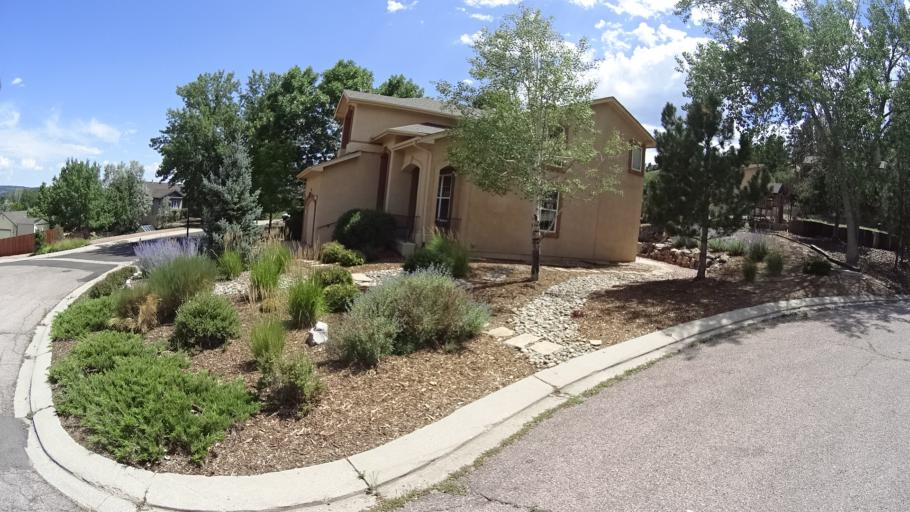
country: US
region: Colorado
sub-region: El Paso County
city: Air Force Academy
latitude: 38.9324
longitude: -104.8348
